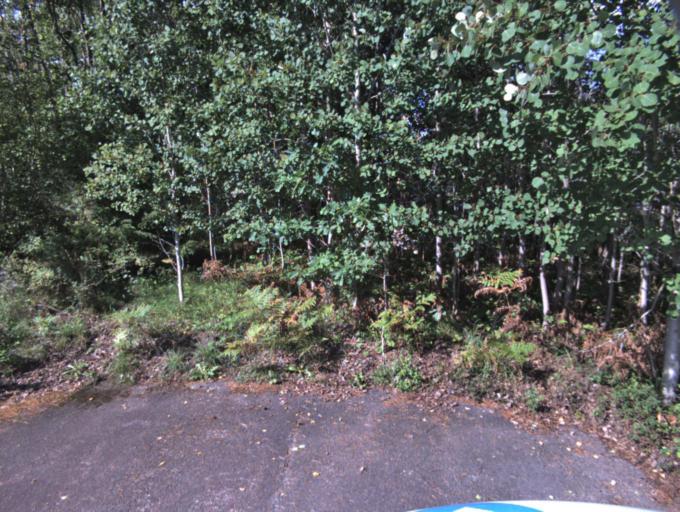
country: SE
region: Vaestra Goetaland
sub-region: Ulricehamns Kommun
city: Ulricehamn
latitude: 57.7999
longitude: 13.3930
